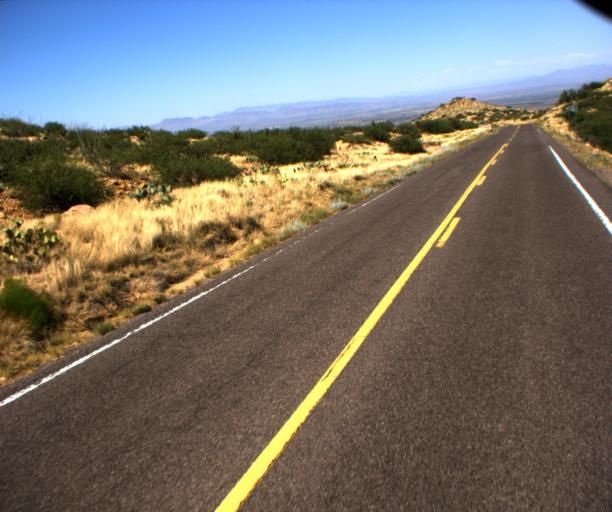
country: US
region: Arizona
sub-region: Graham County
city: Swift Trail Junction
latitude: 32.6847
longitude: -109.7683
